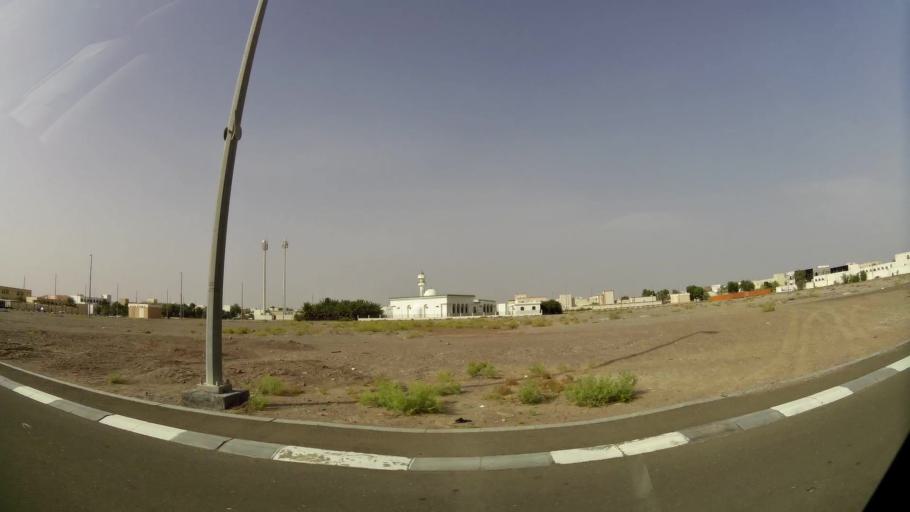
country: AE
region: Abu Dhabi
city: Al Ain
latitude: 24.2070
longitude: 55.5920
